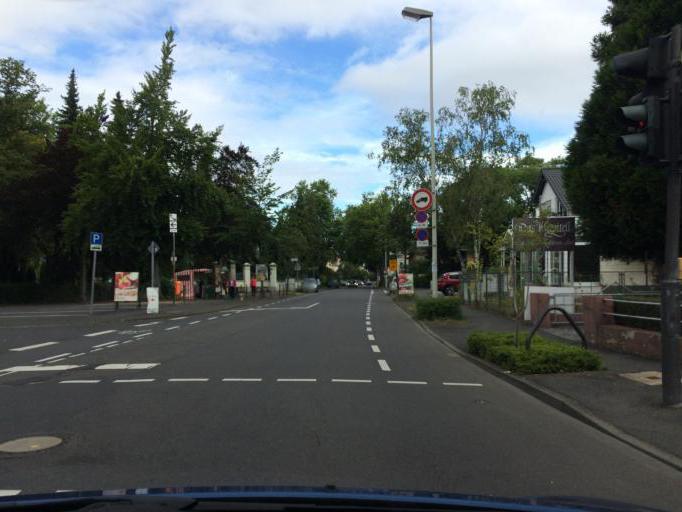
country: DE
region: North Rhine-Westphalia
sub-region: Regierungsbezirk Koln
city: Konigswinter
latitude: 50.6799
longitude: 7.1724
